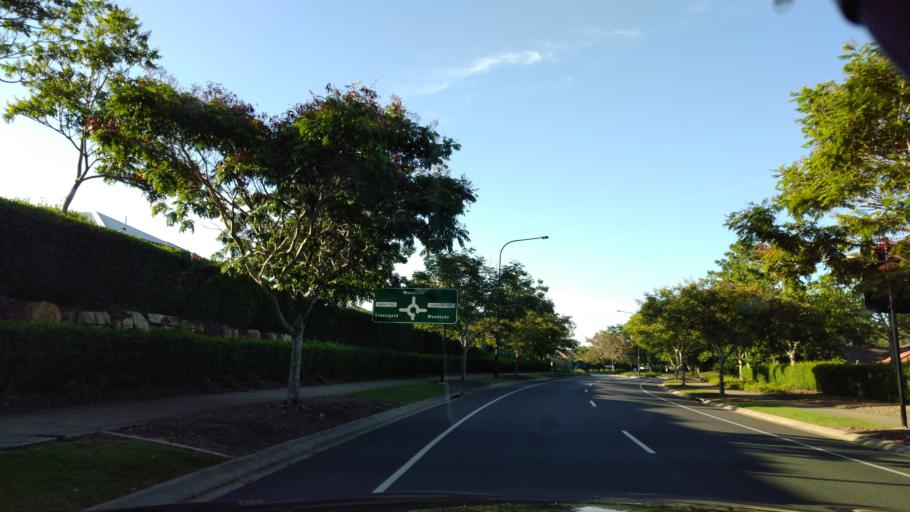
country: AU
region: Queensland
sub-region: Moreton Bay
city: Deception Bay
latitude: -27.2178
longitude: 153.0212
